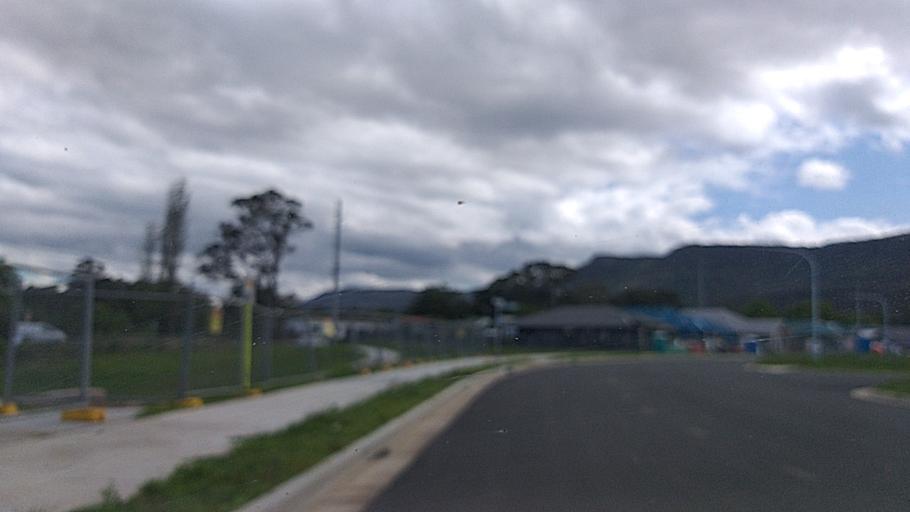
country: AU
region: New South Wales
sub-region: Wollongong
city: Dapto
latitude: -34.4778
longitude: 150.7658
